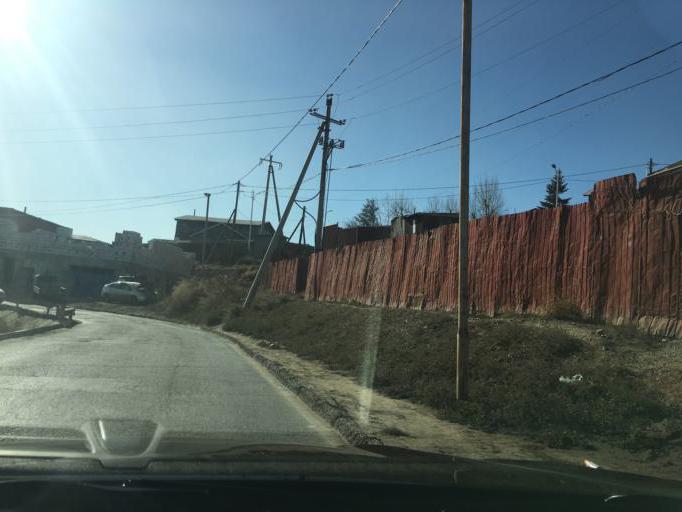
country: MN
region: Ulaanbaatar
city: Ulaanbaatar
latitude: 47.9324
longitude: 106.8796
